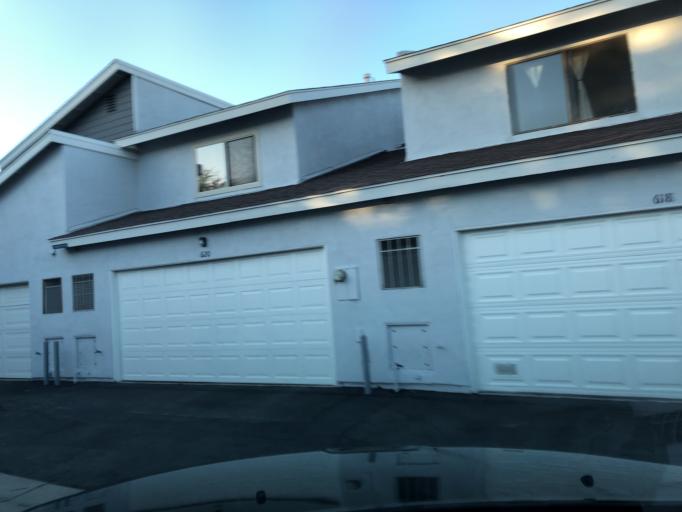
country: US
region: California
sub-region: Orange County
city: Costa Mesa
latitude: 33.6854
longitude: -117.8821
